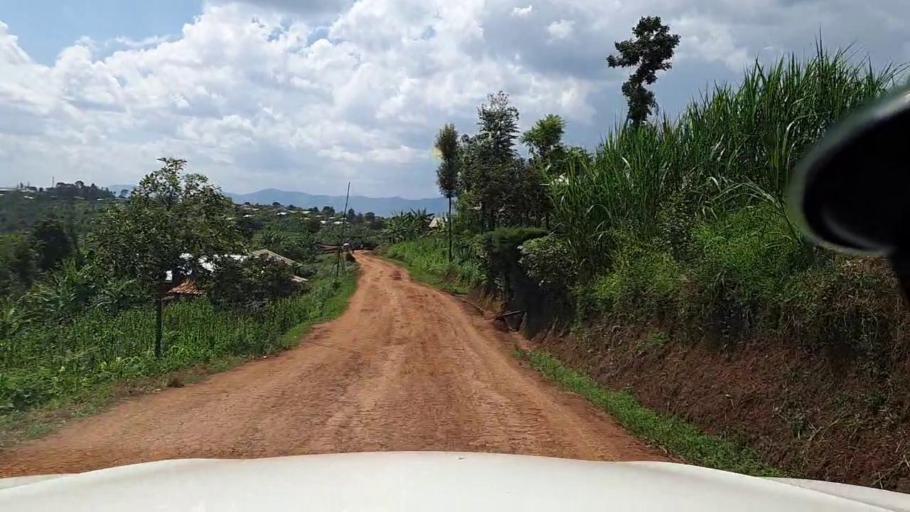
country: RW
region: Kigali
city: Kigali
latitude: -1.8330
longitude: 29.8406
